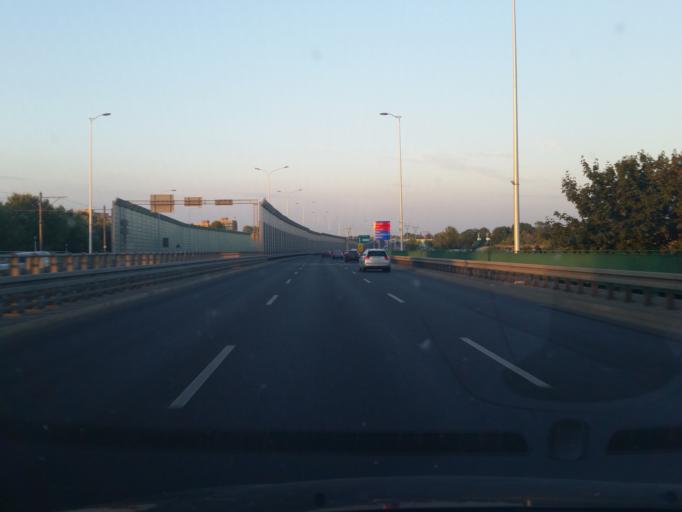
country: PL
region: Masovian Voivodeship
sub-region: Warszawa
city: Bialoleka
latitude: 52.3089
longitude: 20.9562
